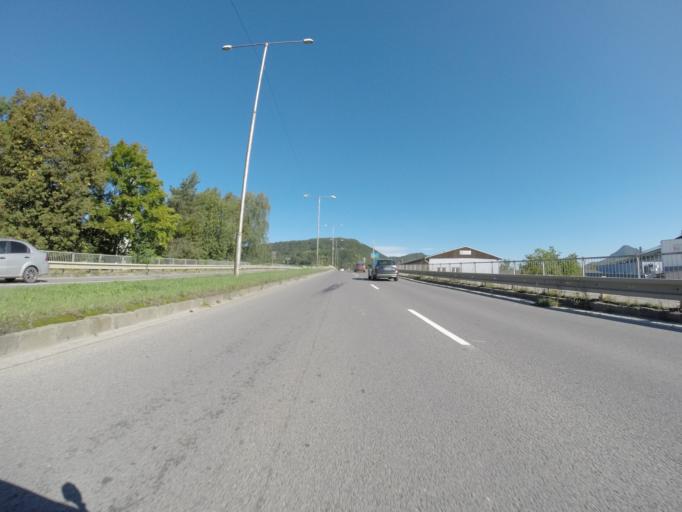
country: SK
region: Trenciansky
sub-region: Okres Povazska Bystrica
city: Povazska Bystrica
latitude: 49.1197
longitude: 18.4379
